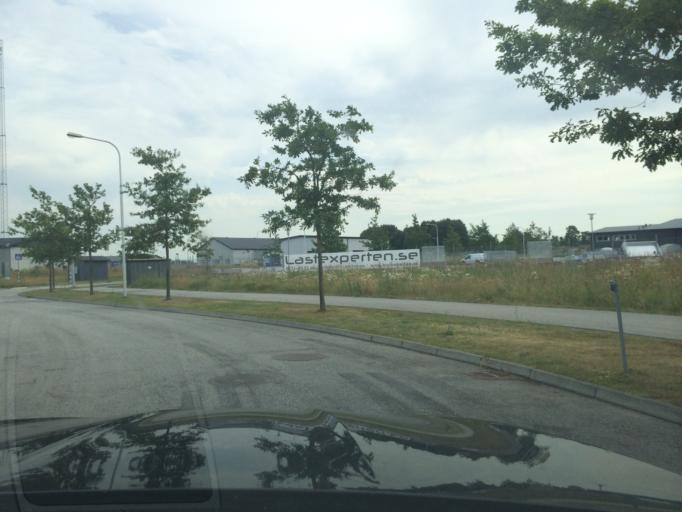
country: SE
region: Skane
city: Bjarred
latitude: 55.7394
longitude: 13.0334
